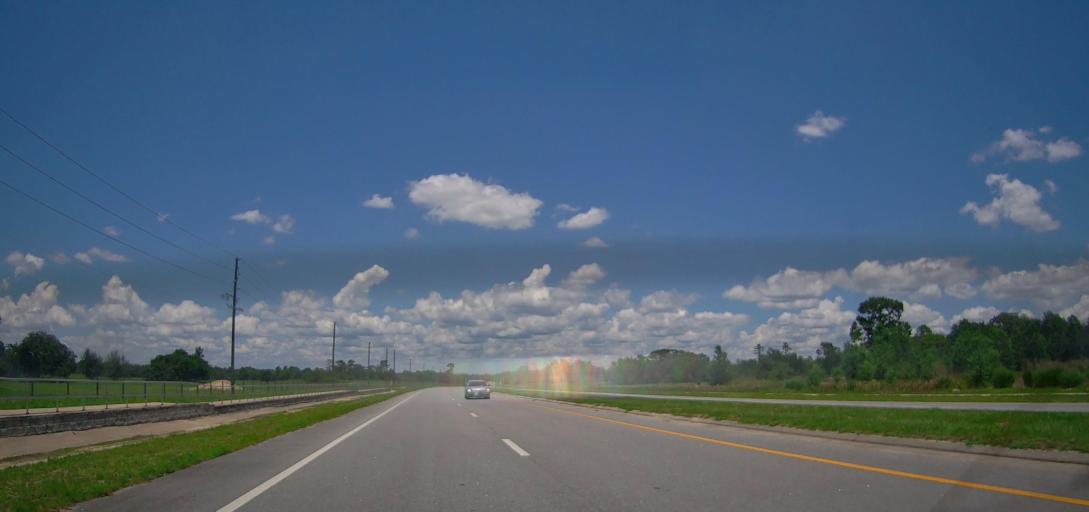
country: US
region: Florida
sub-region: Marion County
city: Belleview
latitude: 29.0487
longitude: -82.0176
